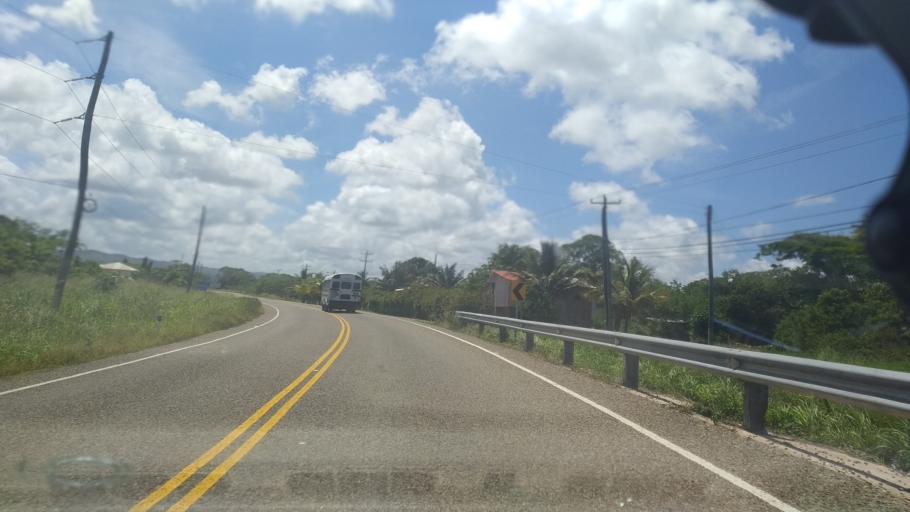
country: BZ
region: Stann Creek
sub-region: Dangriga
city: Dangriga
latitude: 17.0022
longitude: -88.3035
